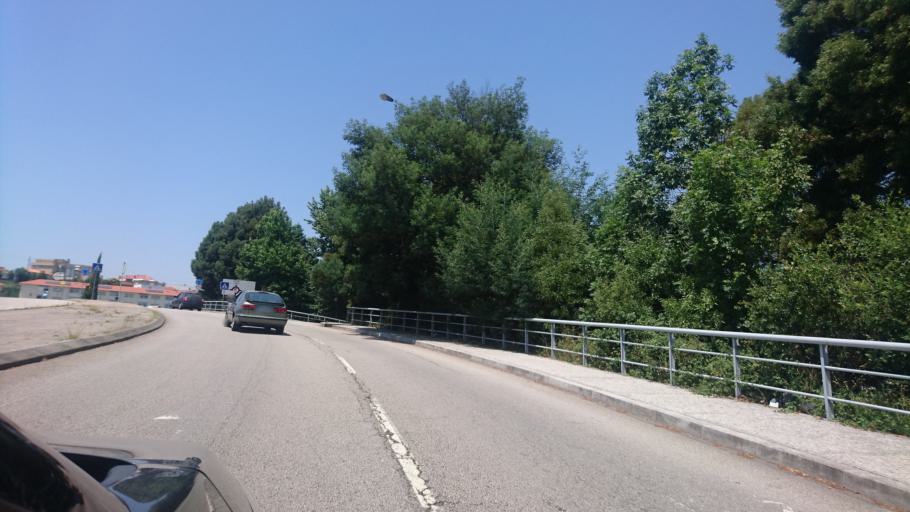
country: PT
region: Porto
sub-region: Gondomar
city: Rio Tinto
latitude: 41.1649
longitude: -8.5765
